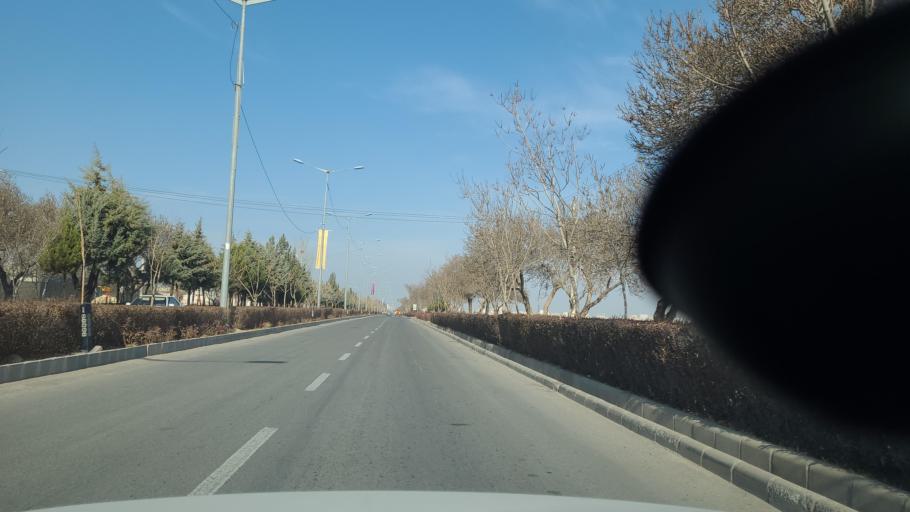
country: IR
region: Razavi Khorasan
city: Fariman
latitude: 35.6819
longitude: 59.8432
